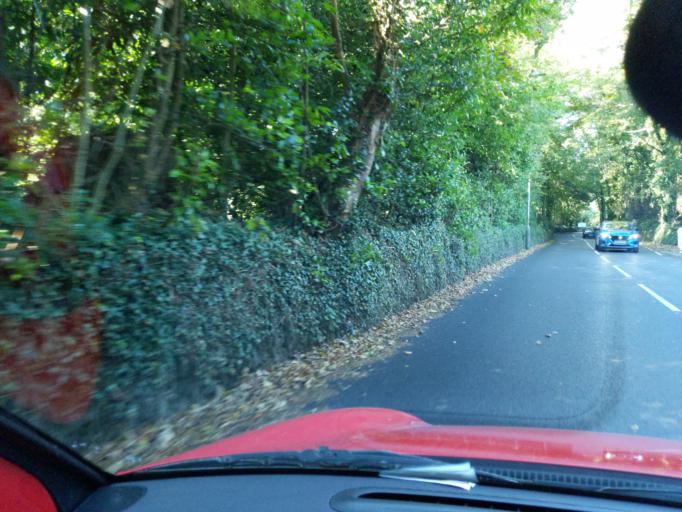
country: GB
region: England
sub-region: Plymouth
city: Plymouth
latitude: 50.4258
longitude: -4.1494
